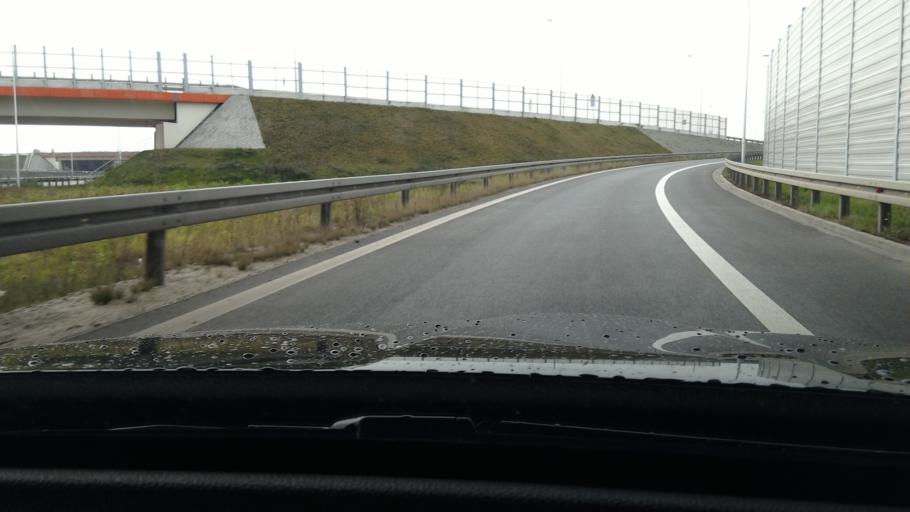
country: PL
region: Masovian Voivodeship
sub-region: Powiat pruszkowski
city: Nowe Grocholice
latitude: 52.1763
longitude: 20.9132
